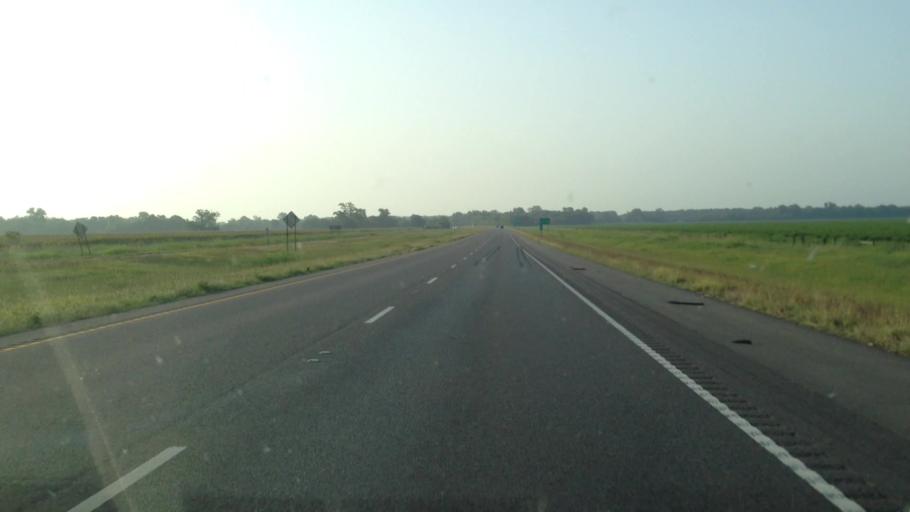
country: US
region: Louisiana
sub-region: Rapides Parish
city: Boyce
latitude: 31.3888
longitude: -92.6880
